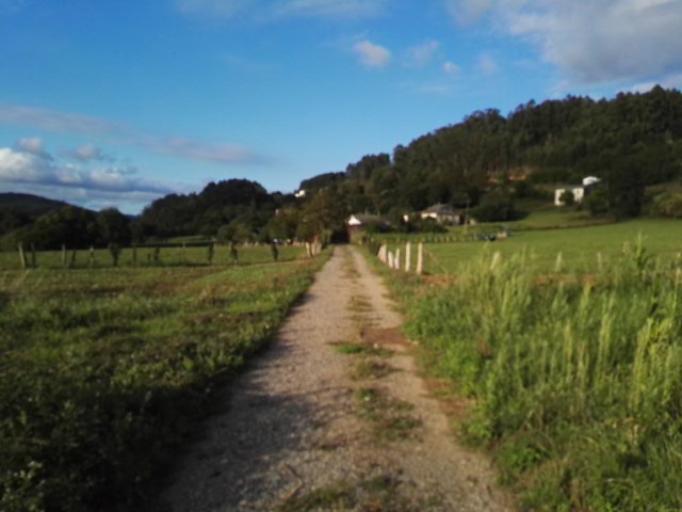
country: ES
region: Galicia
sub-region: Provincia de Lugo
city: Mondonedo
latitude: 43.4295
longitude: -7.3561
